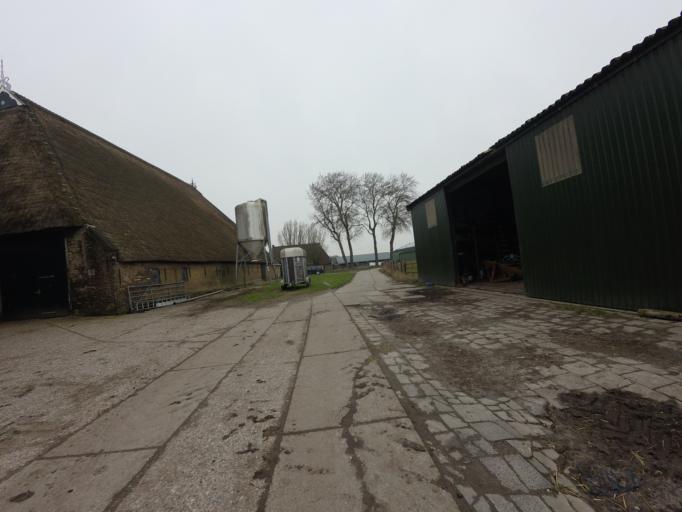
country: NL
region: Friesland
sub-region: Gemeente Franekeradeel
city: Franeker
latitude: 53.1934
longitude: 5.5533
